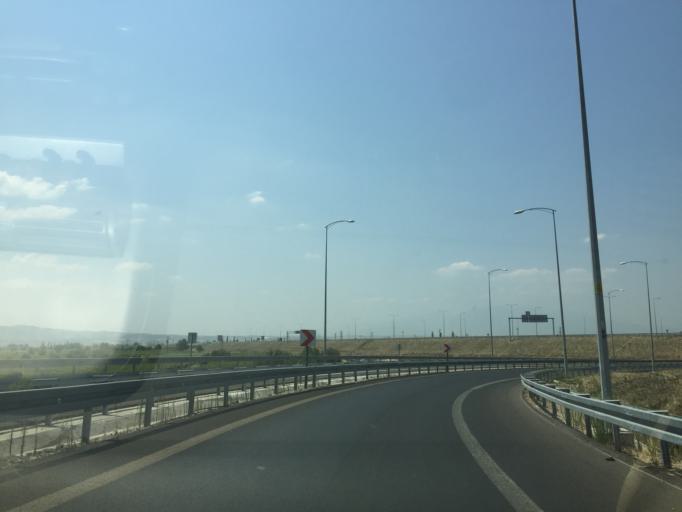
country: TR
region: Manisa
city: Halitpasa
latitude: 38.7658
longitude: 27.6622
